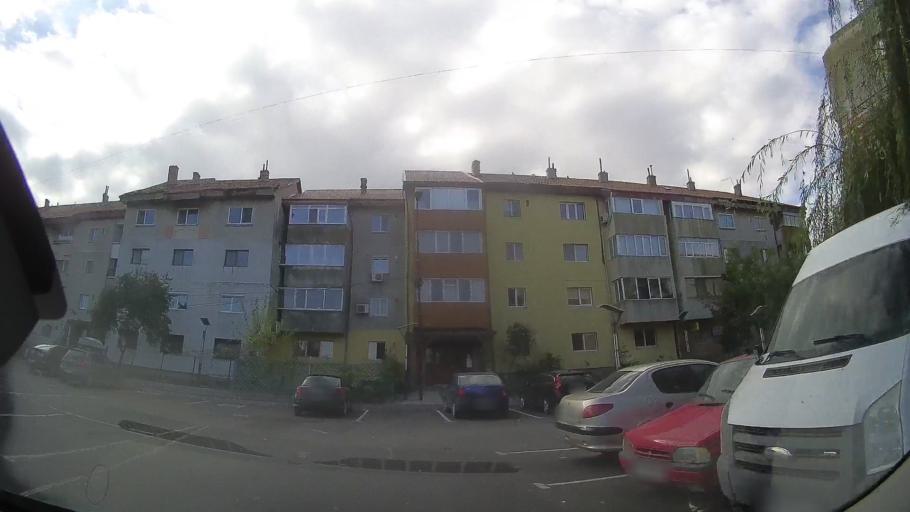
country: RO
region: Constanta
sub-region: Oras Techirghiol
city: Techirghiol
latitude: 44.0548
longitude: 28.6005
